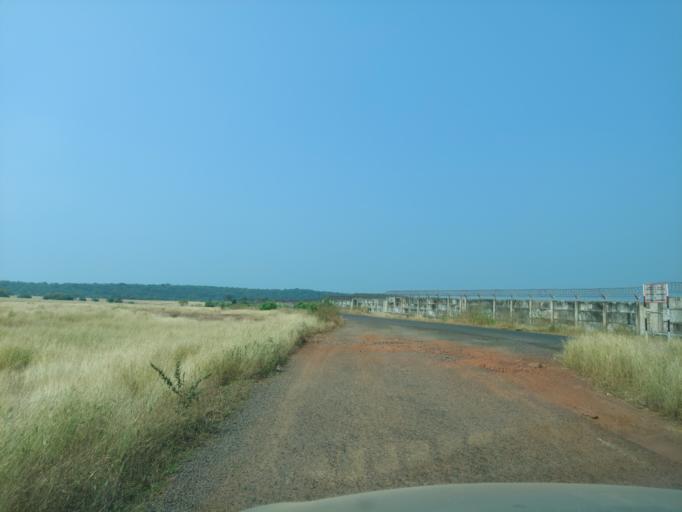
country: IN
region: Maharashtra
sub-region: Sindhudurg
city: Malvan
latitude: 15.9985
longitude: 73.5131
